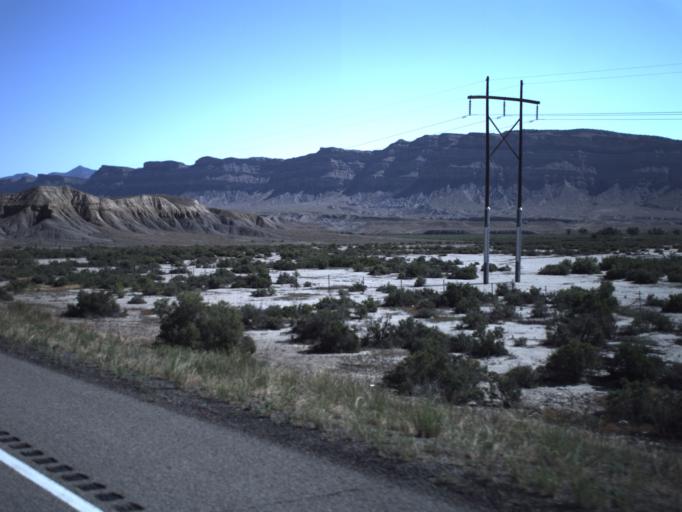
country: US
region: Utah
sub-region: Carbon County
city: East Carbon City
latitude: 39.2455
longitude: -110.3389
